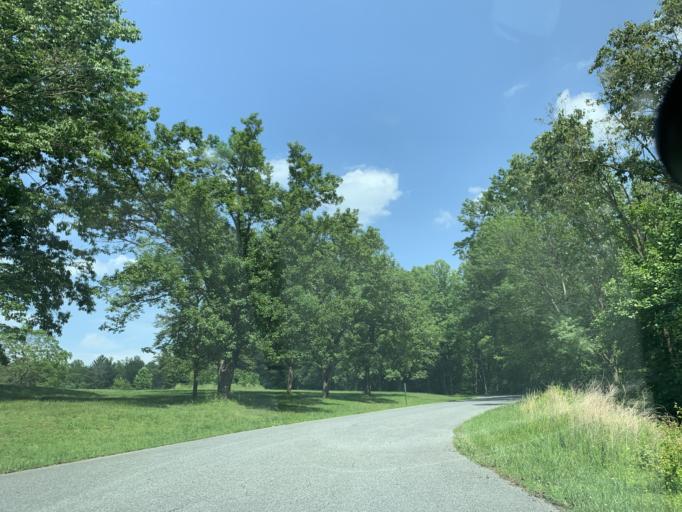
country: US
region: Maryland
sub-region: Carroll County
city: Eldersburg
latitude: 39.3549
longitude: -76.8866
